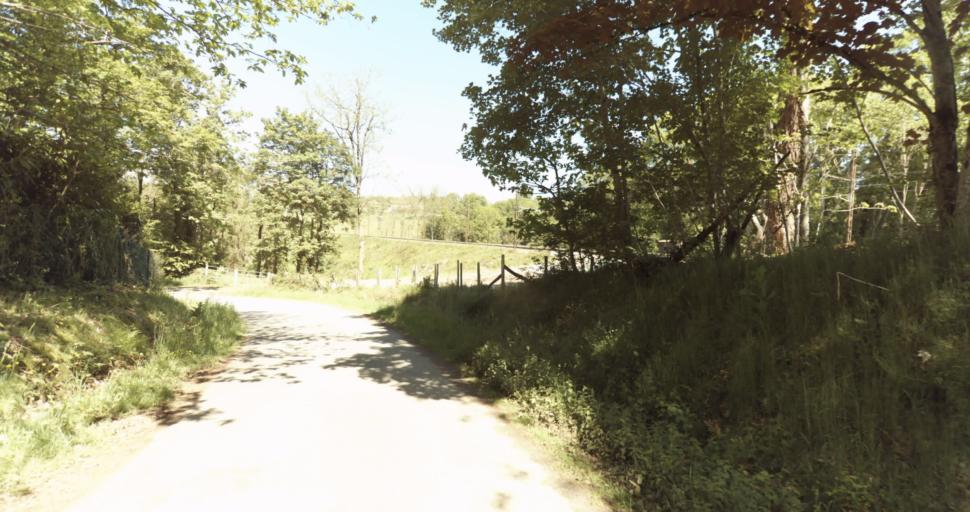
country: FR
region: Limousin
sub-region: Departement de la Haute-Vienne
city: Le Vigen
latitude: 45.7497
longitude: 1.3074
